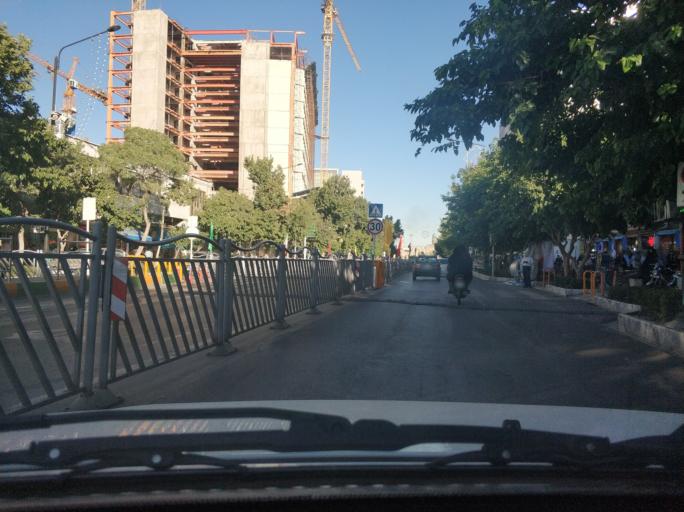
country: IR
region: Razavi Khorasan
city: Mashhad
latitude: 36.2935
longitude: 59.6105
